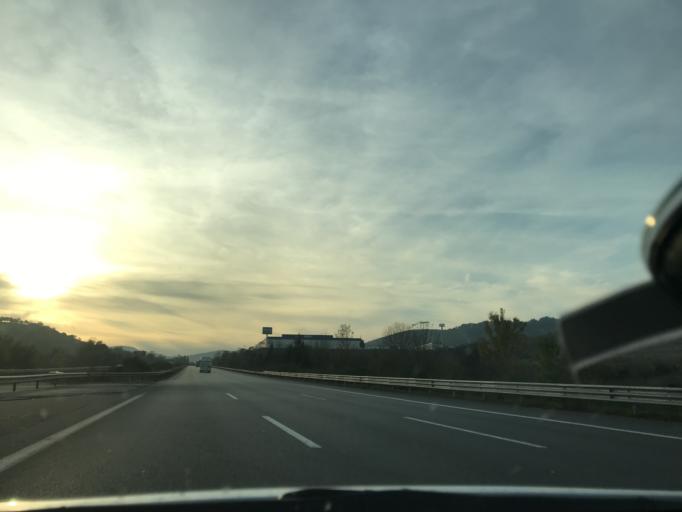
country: TR
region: Duzce
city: Gumusova
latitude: 40.8412
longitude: 30.9714
